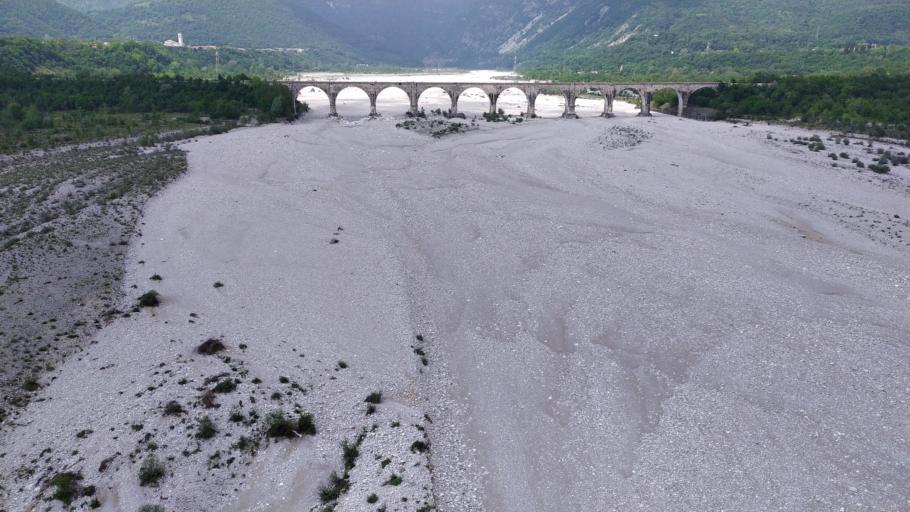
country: IT
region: Friuli Venezia Giulia
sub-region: Provincia di Pordenone
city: Vajont
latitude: 46.1495
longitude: 12.6767
